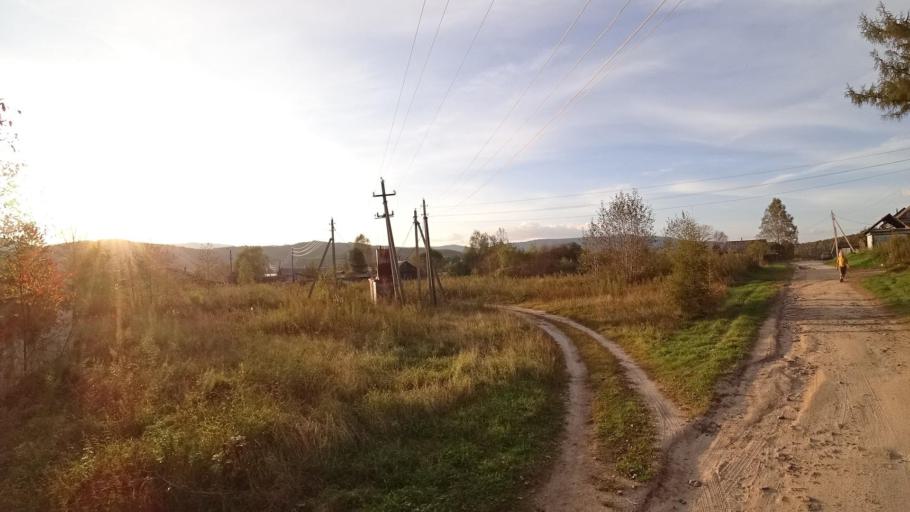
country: RU
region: Jewish Autonomous Oblast
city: Kul'dur
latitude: 49.2090
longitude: 131.6411
